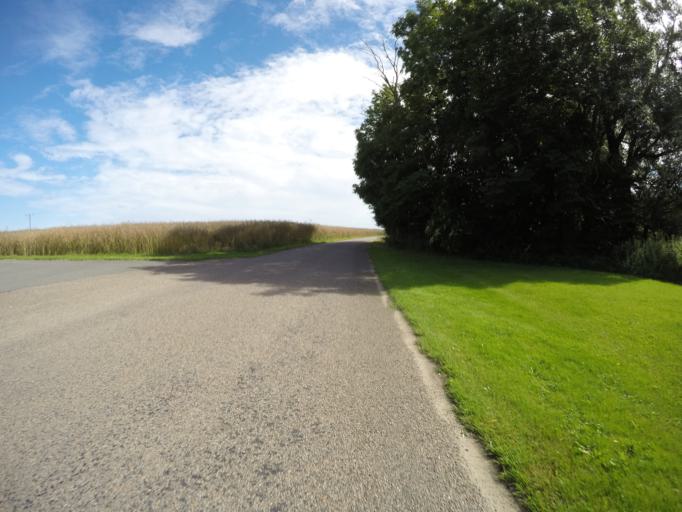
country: SE
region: Skane
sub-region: Simrishamns Kommun
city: Simrishamn
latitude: 55.4992
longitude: 14.2307
